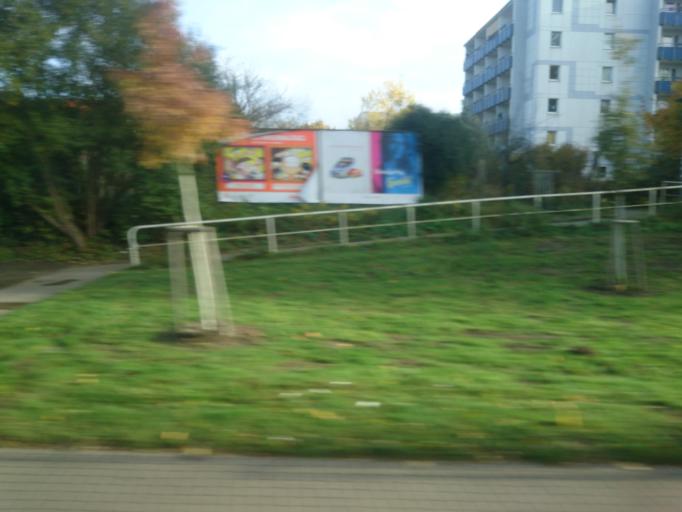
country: DE
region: Mecklenburg-Vorpommern
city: Rostock
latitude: 54.0760
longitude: 12.1019
